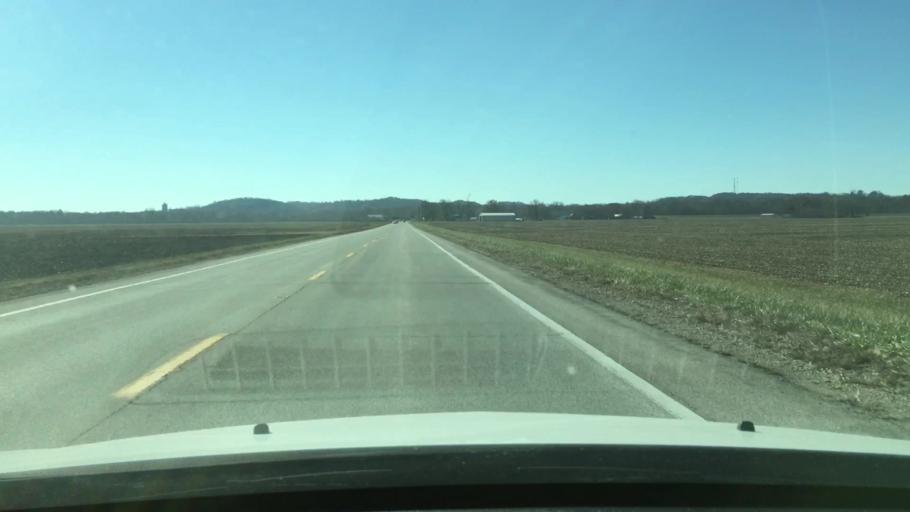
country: US
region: Missouri
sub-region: Pike County
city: Louisiana
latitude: 39.4715
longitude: -91.0241
